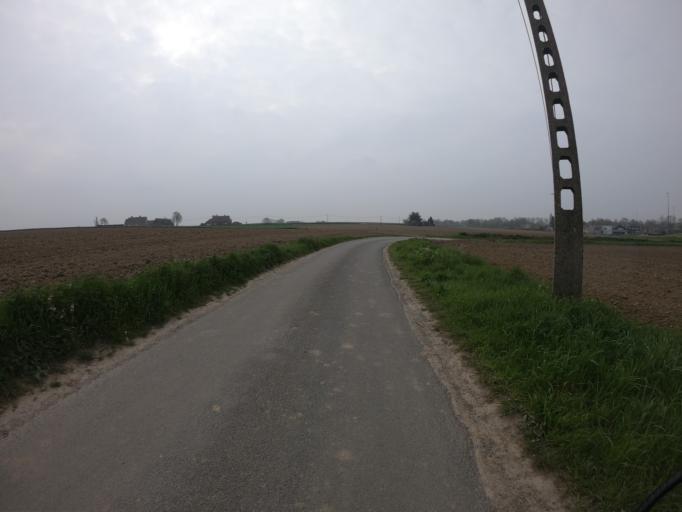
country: BE
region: Flanders
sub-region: Provincie West-Vlaanderen
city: Zwevegem
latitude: 50.7998
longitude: 3.3696
